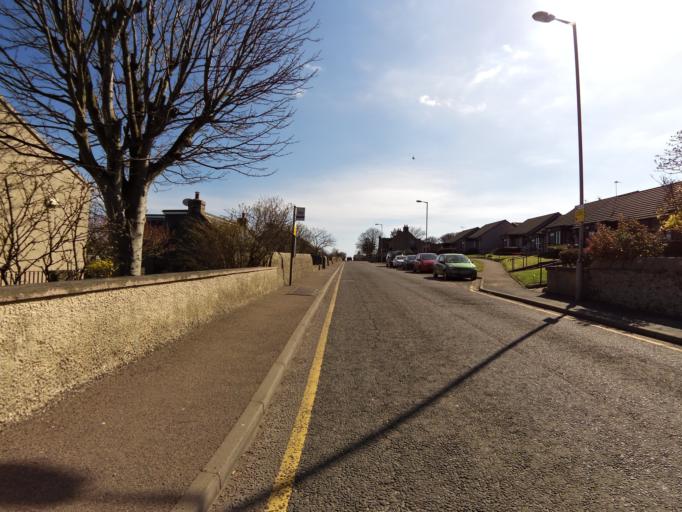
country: GB
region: Scotland
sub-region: Aberdeen City
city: Aberdeen
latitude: 57.1012
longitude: -2.0802
